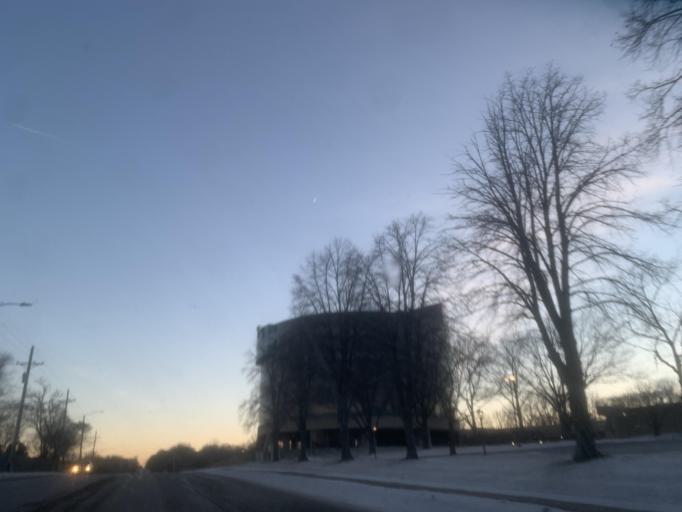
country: US
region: Nebraska
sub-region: Douglas County
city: Ralston
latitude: 41.2720
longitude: -96.0622
